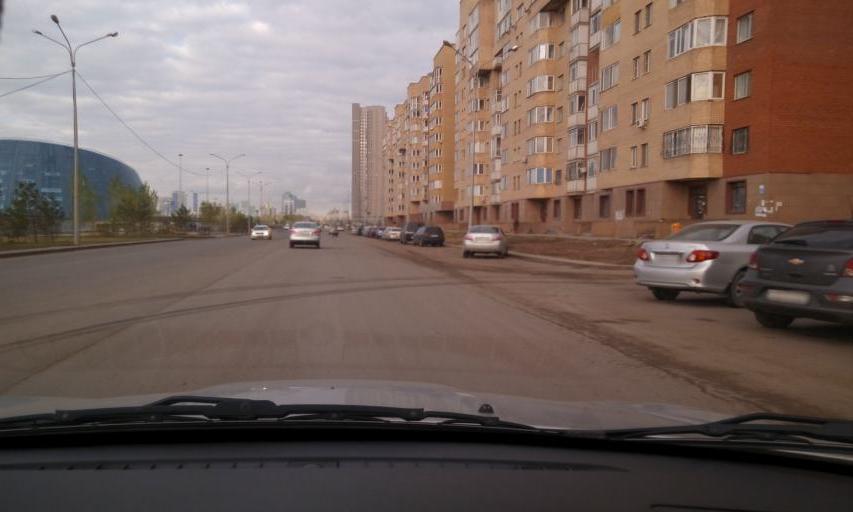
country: KZ
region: Astana Qalasy
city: Astana
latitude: 51.1232
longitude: 71.4790
